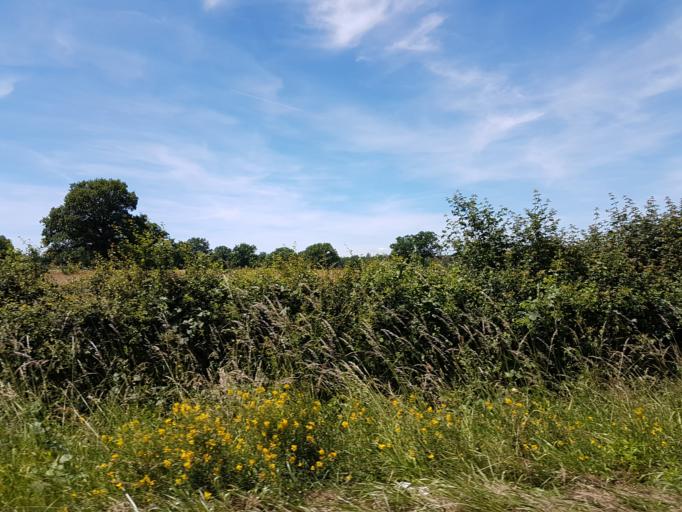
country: FR
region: Bourgogne
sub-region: Departement de Saone-et-Loire
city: Epinac
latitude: 47.0028
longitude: 4.4763
